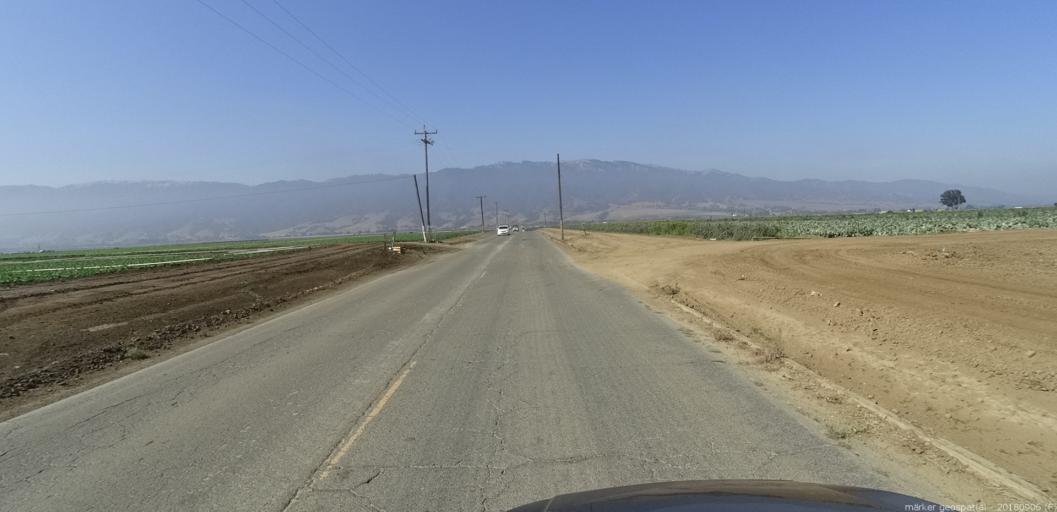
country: US
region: California
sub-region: Monterey County
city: Chualar
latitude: 36.5636
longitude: -121.5202
